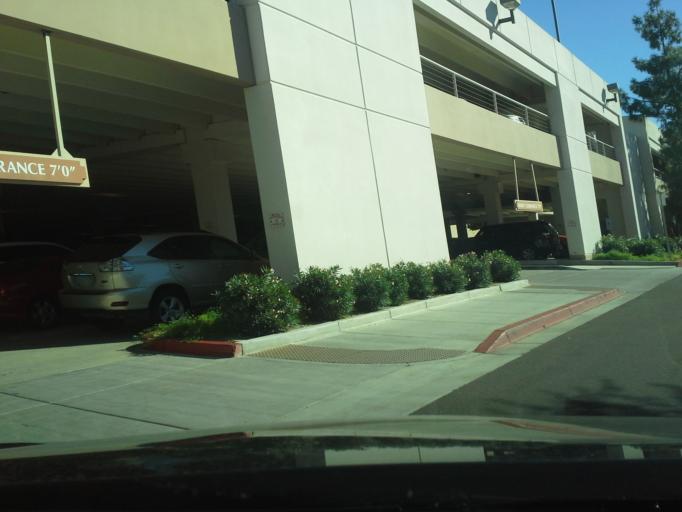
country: US
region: Arizona
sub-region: Maricopa County
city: Paradise Valley
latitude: 33.6042
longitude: -111.9849
